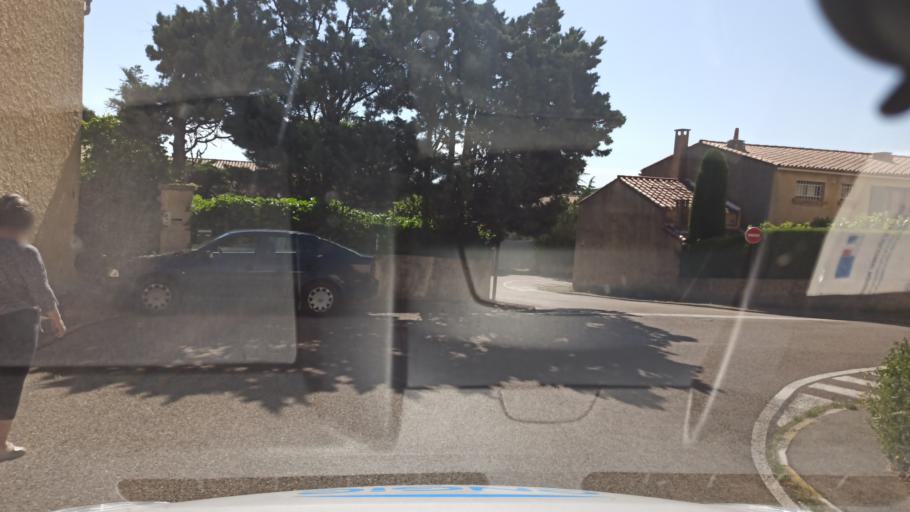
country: FR
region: Languedoc-Roussillon
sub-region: Departement du Gard
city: Villeneuve-les-Avignon
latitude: 43.9760
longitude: 4.7766
